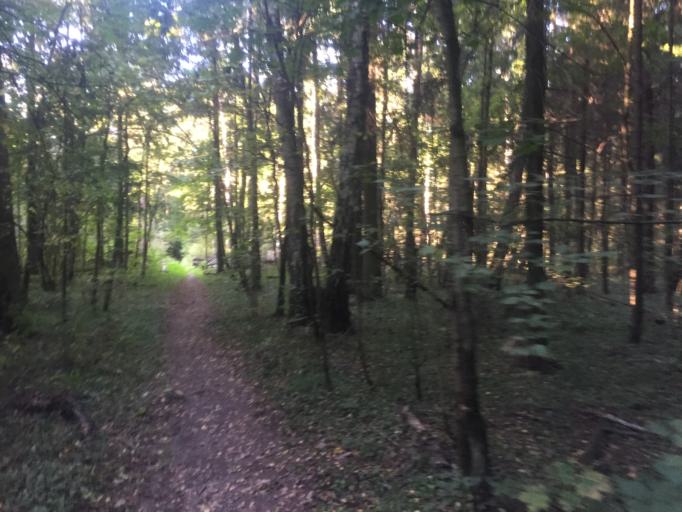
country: RU
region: Moscow
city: Gol'yanovo
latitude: 55.8476
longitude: 37.7874
